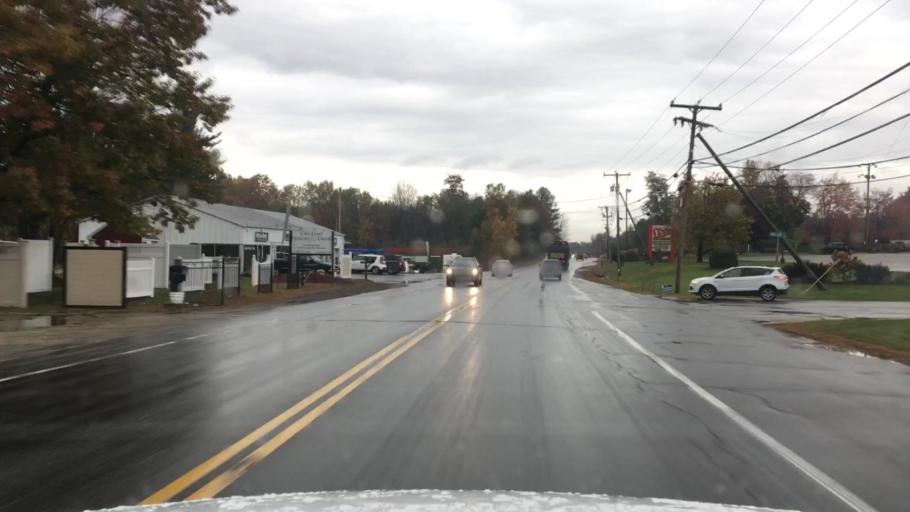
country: US
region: New Hampshire
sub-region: Strafford County
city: Somersworth
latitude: 43.2373
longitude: -70.8982
